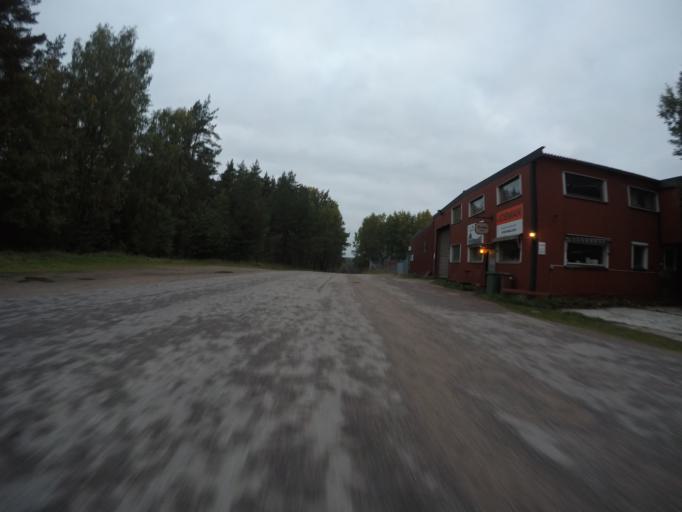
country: SE
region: Vaestmanland
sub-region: Kungsors Kommun
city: Kungsoer
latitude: 59.4059
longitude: 16.1176
